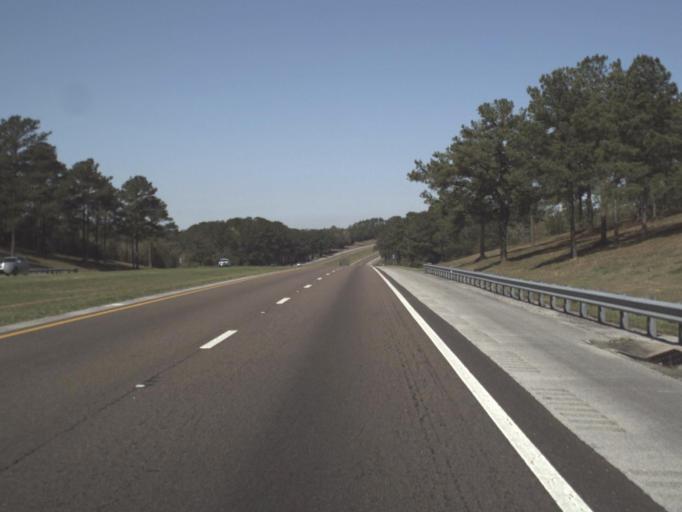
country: US
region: Florida
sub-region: Walton County
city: DeFuniak Springs
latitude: 30.7247
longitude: -86.2007
